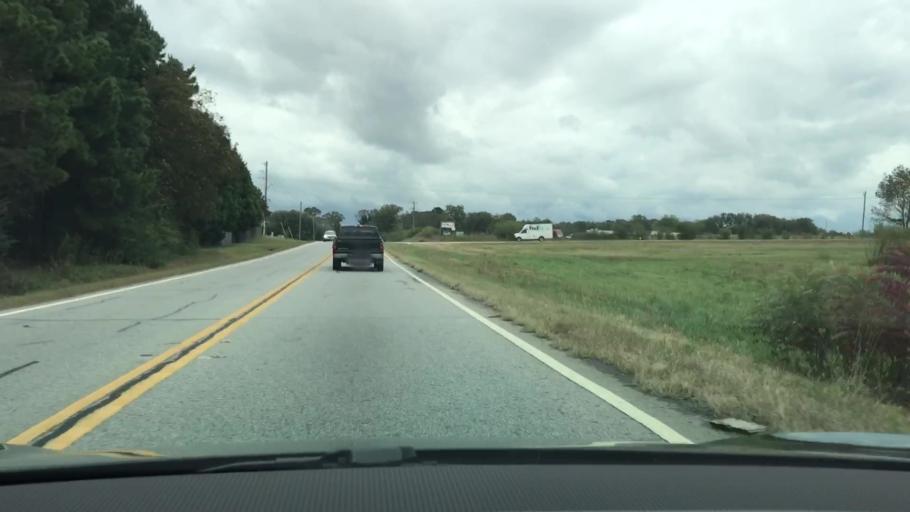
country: US
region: Georgia
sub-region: Oconee County
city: Watkinsville
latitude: 33.8419
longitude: -83.3870
